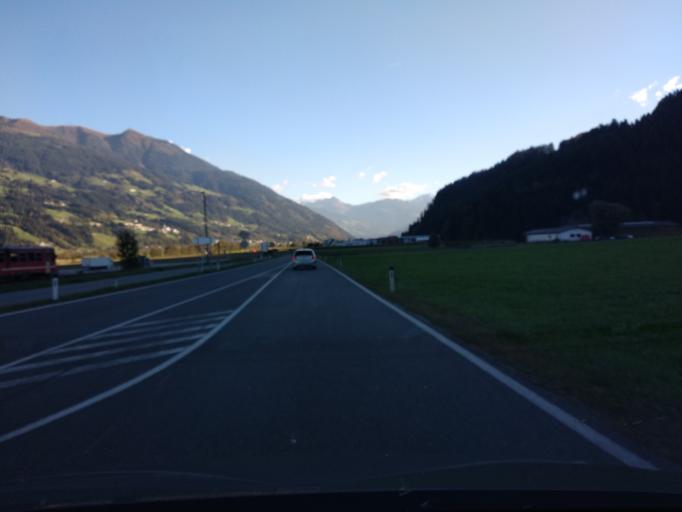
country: AT
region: Tyrol
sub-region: Politischer Bezirk Schwaz
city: Schlitters
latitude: 47.3744
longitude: 11.8450
